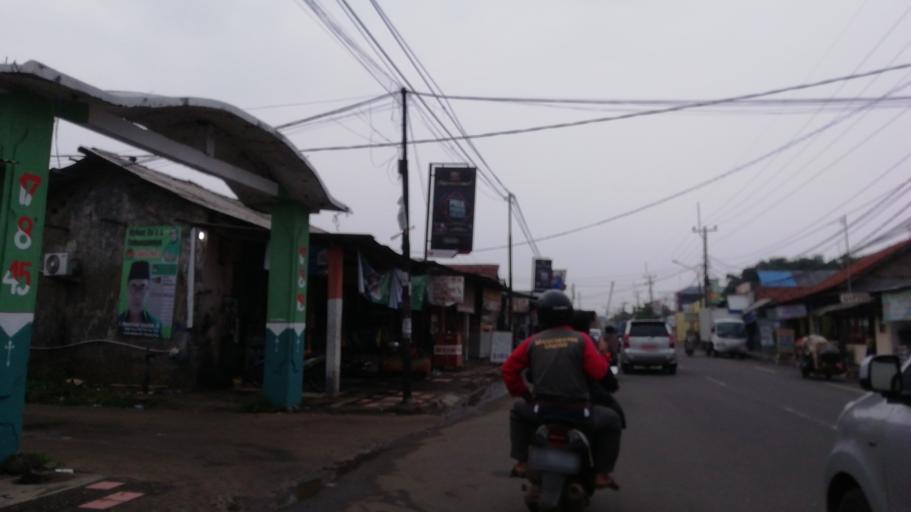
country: ID
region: West Java
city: Cibinong
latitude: -6.4998
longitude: 106.8105
